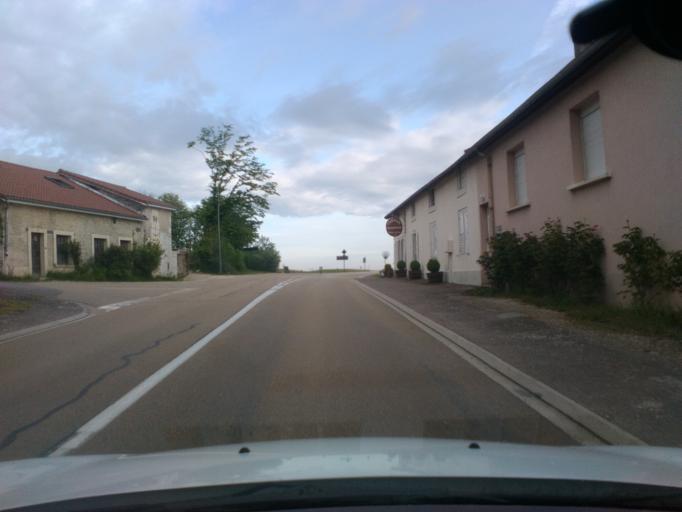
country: FR
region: Champagne-Ardenne
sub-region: Departement de la Haute-Marne
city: Lavilleneuve-au-Roi
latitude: 48.2264
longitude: 4.8857
